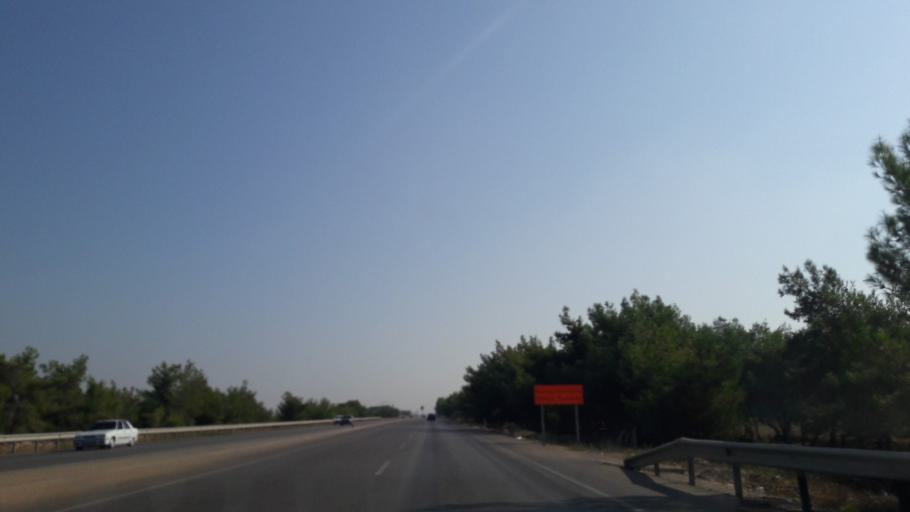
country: TR
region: Adana
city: Yuregir
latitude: 37.0861
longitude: 35.4851
